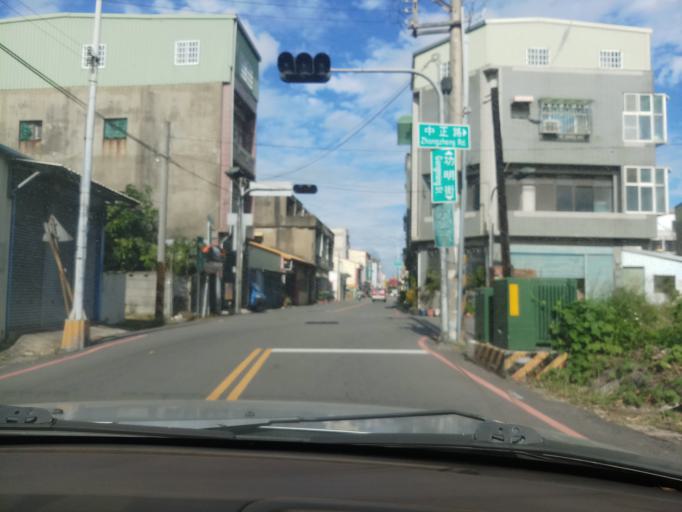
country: TW
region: Taiwan
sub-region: Miaoli
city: Miaoli
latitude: 24.6830
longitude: 120.8633
